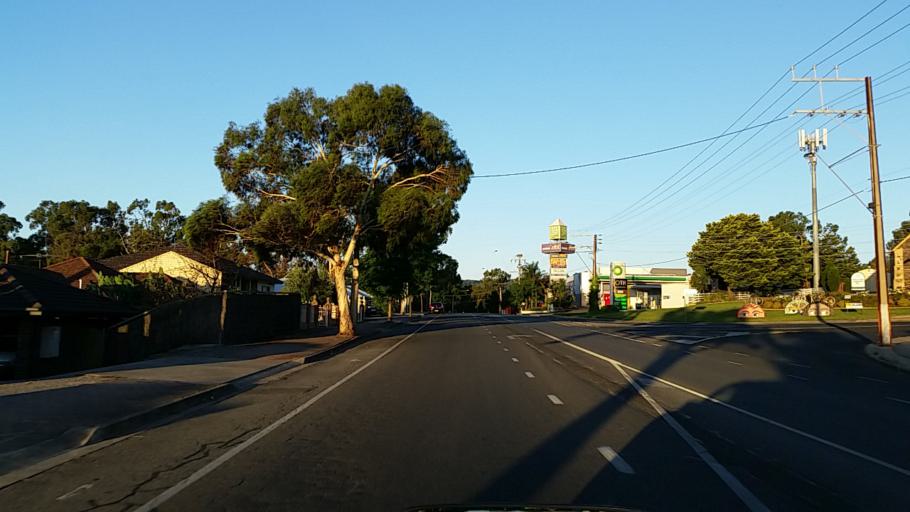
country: AU
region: South Australia
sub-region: Campbelltown
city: Athelstone
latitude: -34.8723
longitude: 138.6992
